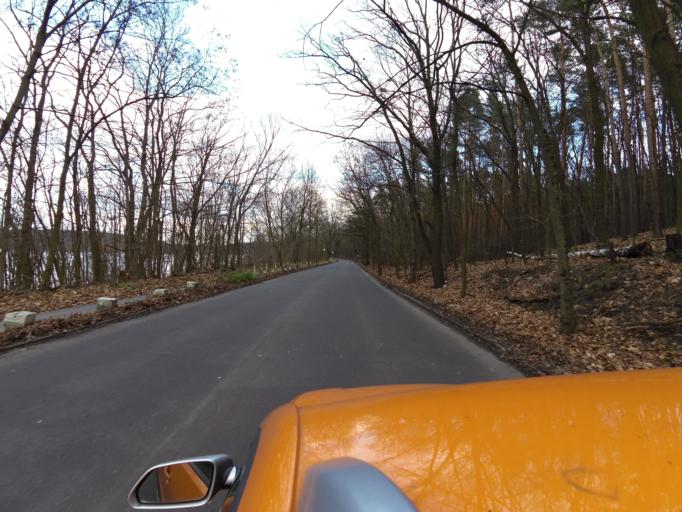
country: DE
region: Berlin
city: Gatow
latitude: 52.4961
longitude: 13.2010
